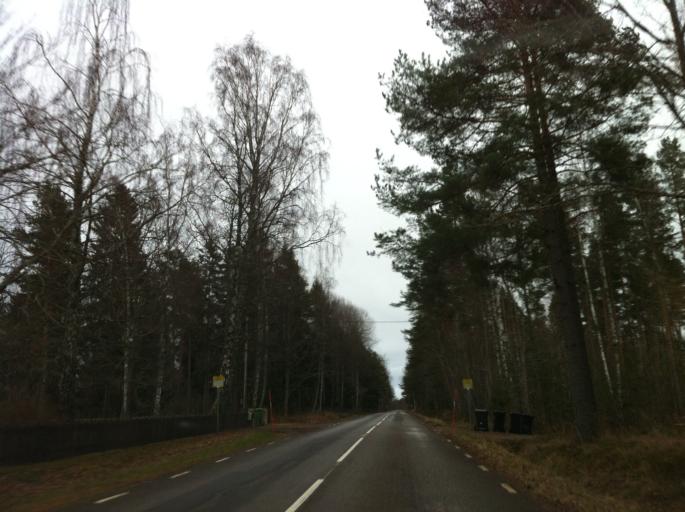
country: SE
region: Kalmar
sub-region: Vasterviks Kommun
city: Vaestervik
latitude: 57.8193
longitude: 16.5744
